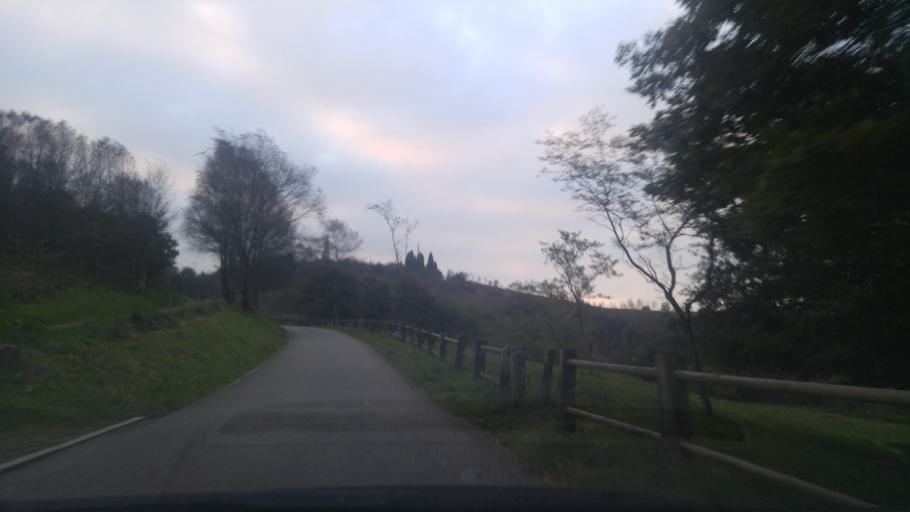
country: ES
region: Asturias
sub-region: Province of Asturias
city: Oviedo
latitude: 43.3845
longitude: -5.8571
